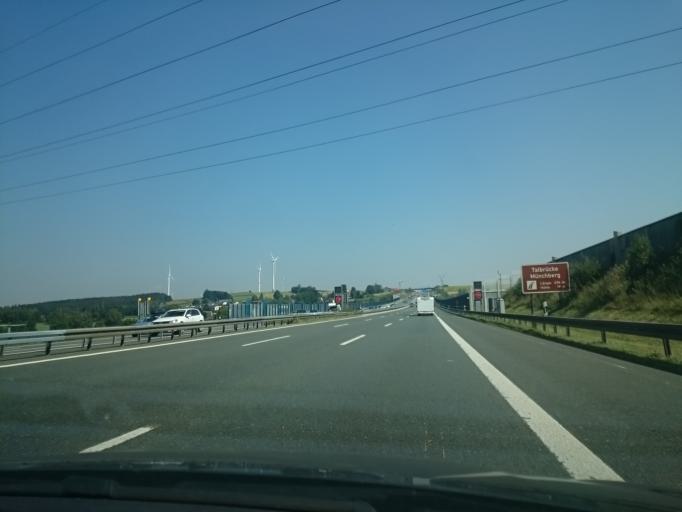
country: DE
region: Bavaria
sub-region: Upper Franconia
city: Munchberg
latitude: 50.1902
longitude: 11.7651
